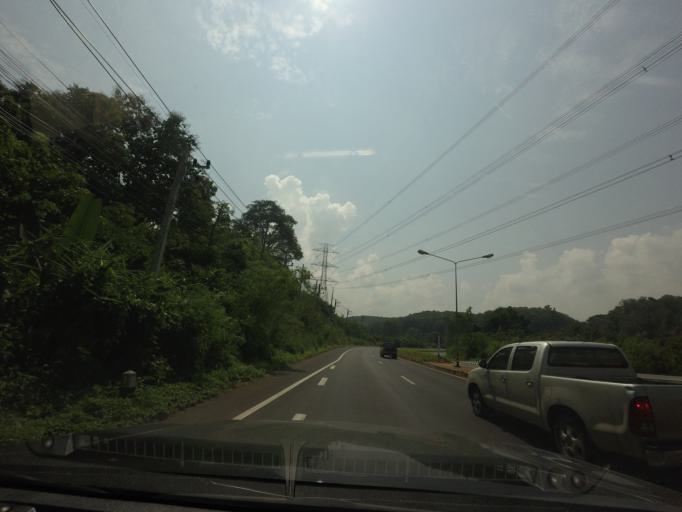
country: TH
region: Phrae
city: Den Chai
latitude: 17.8883
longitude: 100.0492
